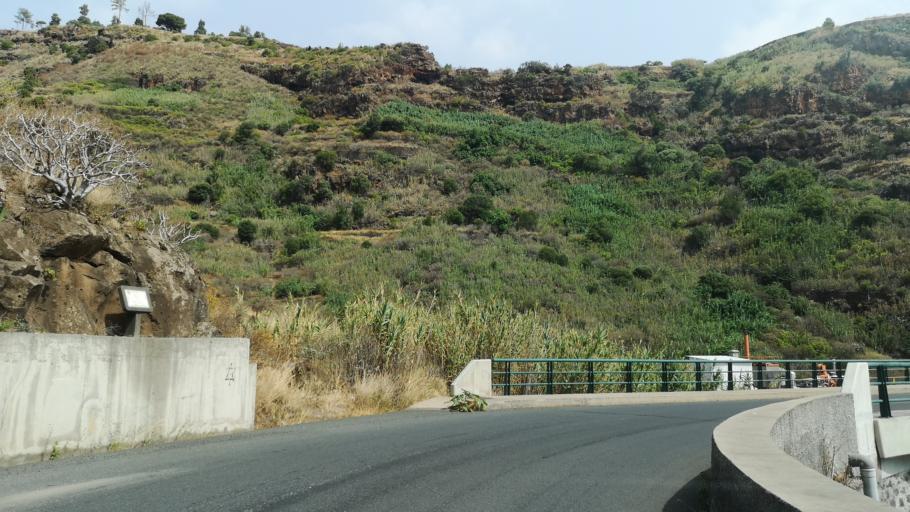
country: PT
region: Madeira
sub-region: Santa Cruz
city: Santa Cruz
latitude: 32.6617
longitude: -16.8135
